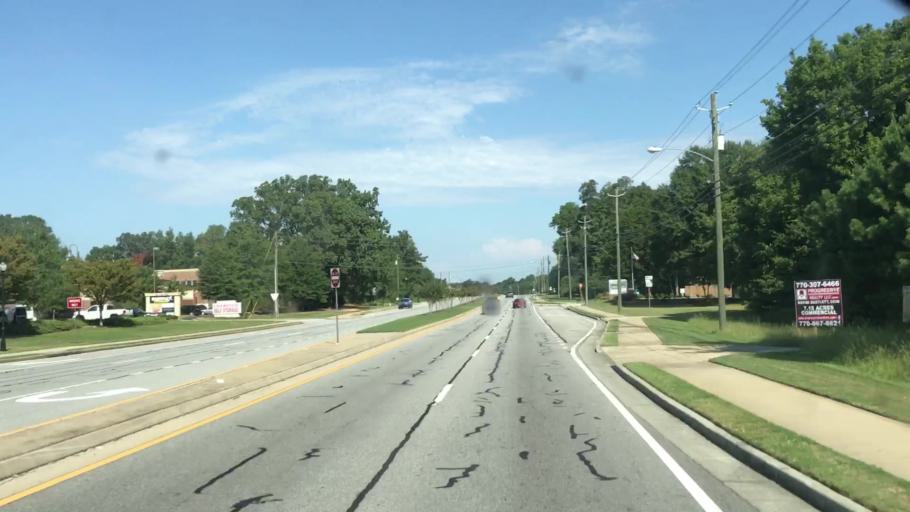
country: US
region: Georgia
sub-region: Gwinnett County
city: Grayson
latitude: 33.8871
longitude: -83.9456
